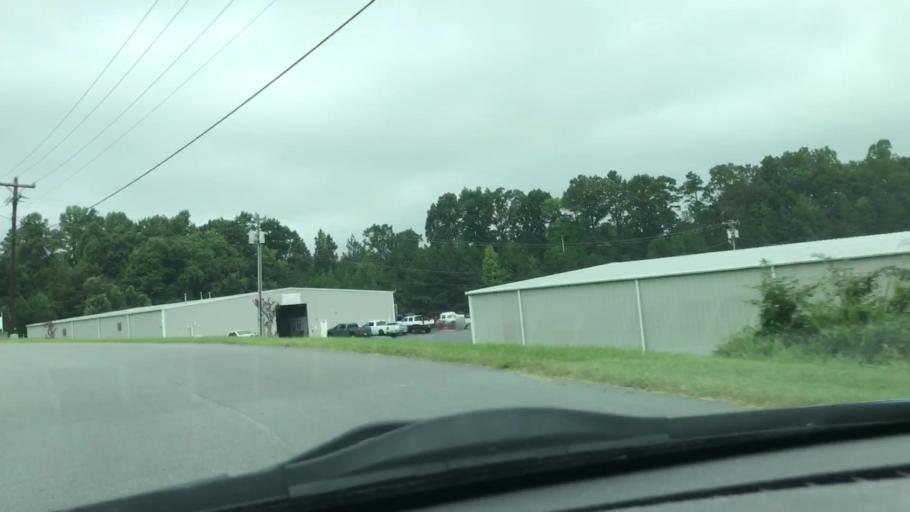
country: US
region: North Carolina
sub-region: Randolph County
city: Randleman
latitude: 35.8075
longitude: -79.8128
